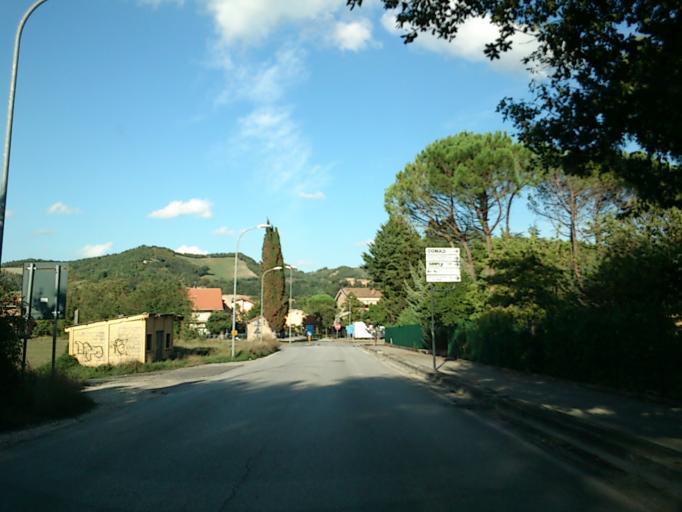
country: IT
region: The Marches
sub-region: Provincia di Pesaro e Urbino
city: Urbania
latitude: 43.6743
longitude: 12.5125
